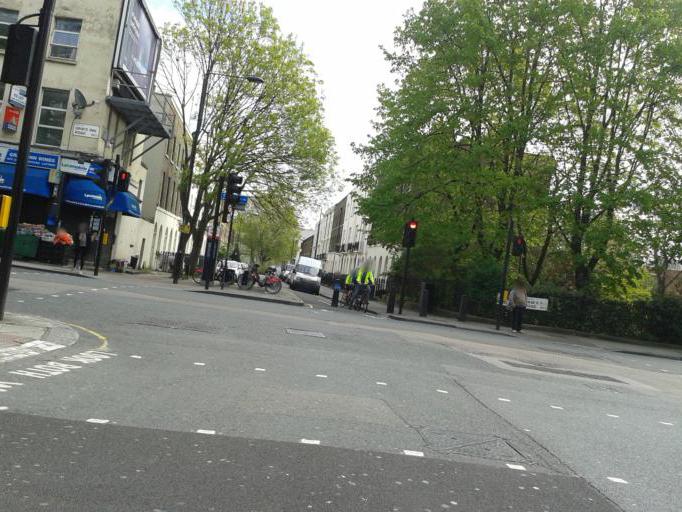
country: GB
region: England
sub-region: Greater London
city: Clerkenwell
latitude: 51.5272
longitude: -0.1187
